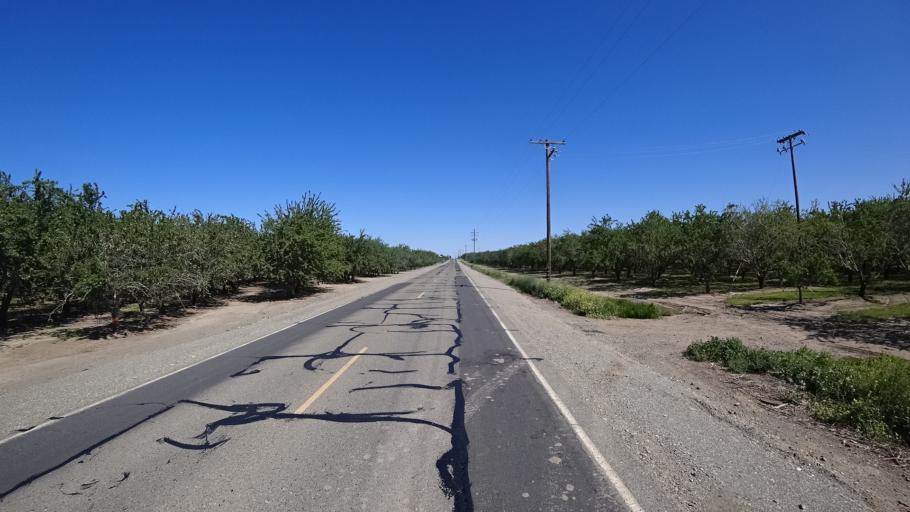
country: US
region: California
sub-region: Glenn County
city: Hamilton City
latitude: 39.7335
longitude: -122.1043
